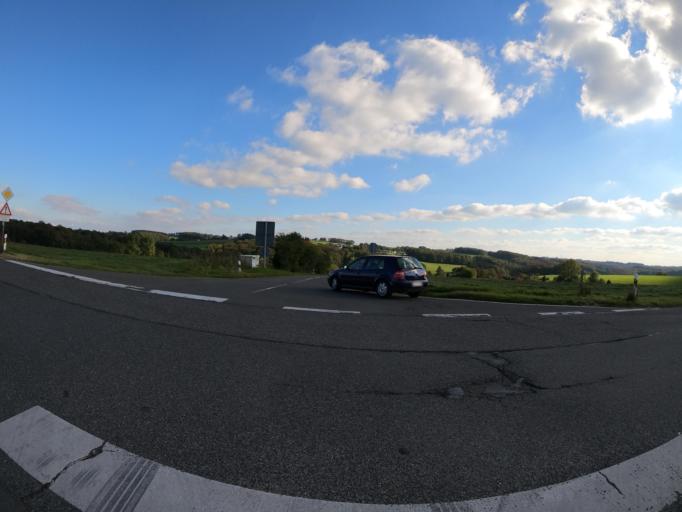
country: DE
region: North Rhine-Westphalia
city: Radevormwald
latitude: 51.2289
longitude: 7.3411
